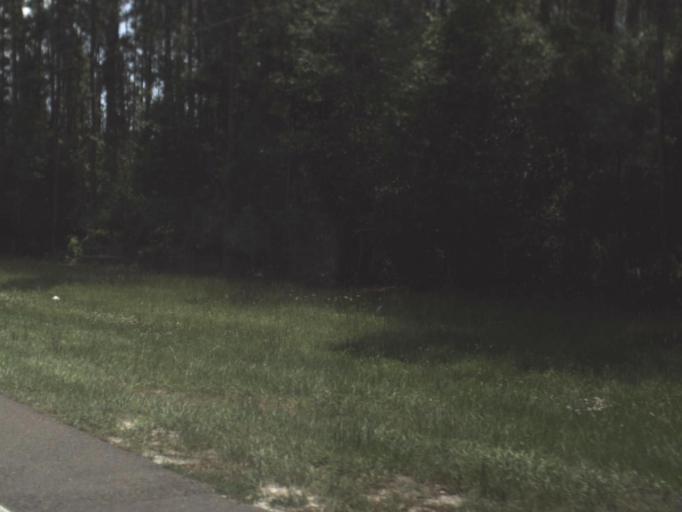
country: US
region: Florida
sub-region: Clay County
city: Keystone Heights
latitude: 29.8169
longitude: -82.0628
